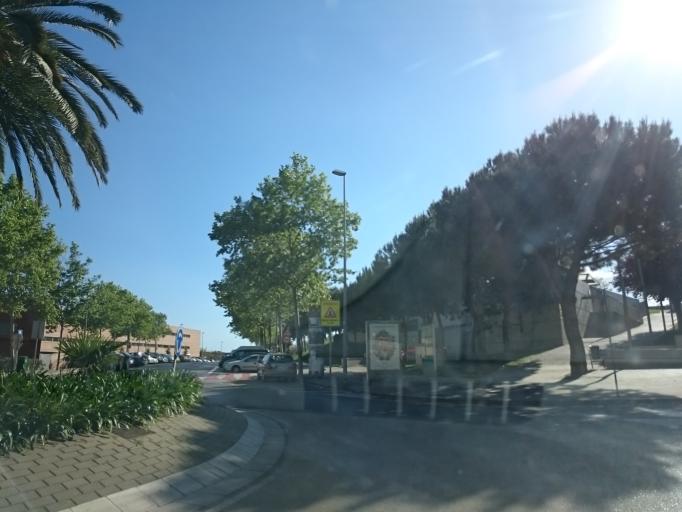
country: ES
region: Catalonia
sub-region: Provincia de Barcelona
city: Viladecans
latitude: 41.3184
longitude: 2.0059
